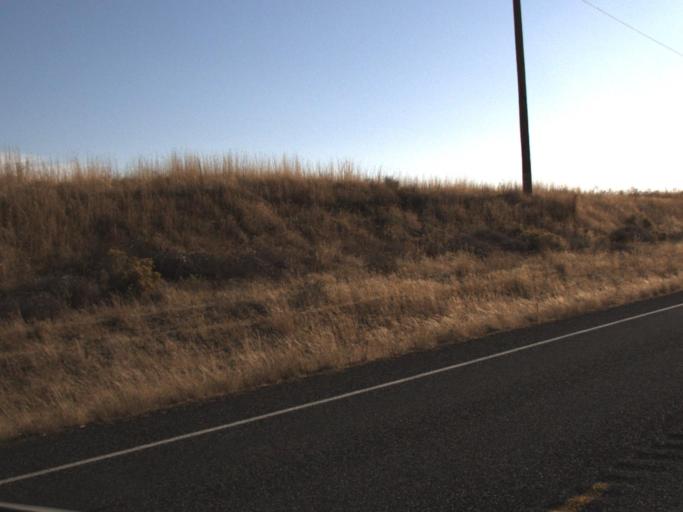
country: US
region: Washington
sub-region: Walla Walla County
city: Burbank
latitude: 46.2829
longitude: -118.7485
